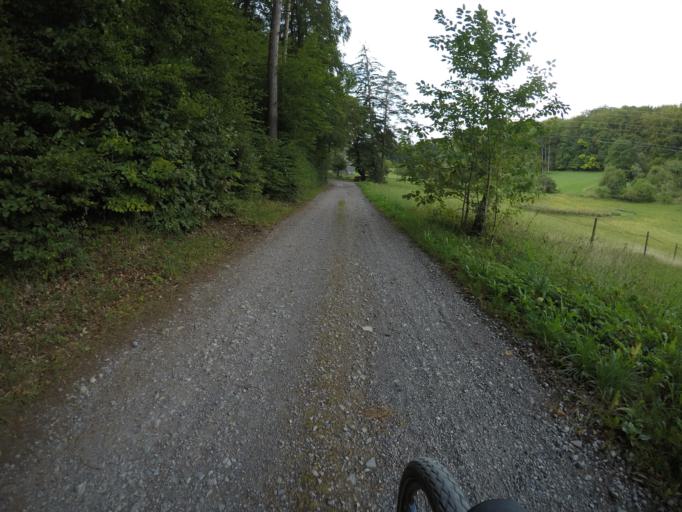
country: DE
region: Baden-Wuerttemberg
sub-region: Karlsruhe Region
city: Simmozheim
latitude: 48.7376
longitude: 8.8145
